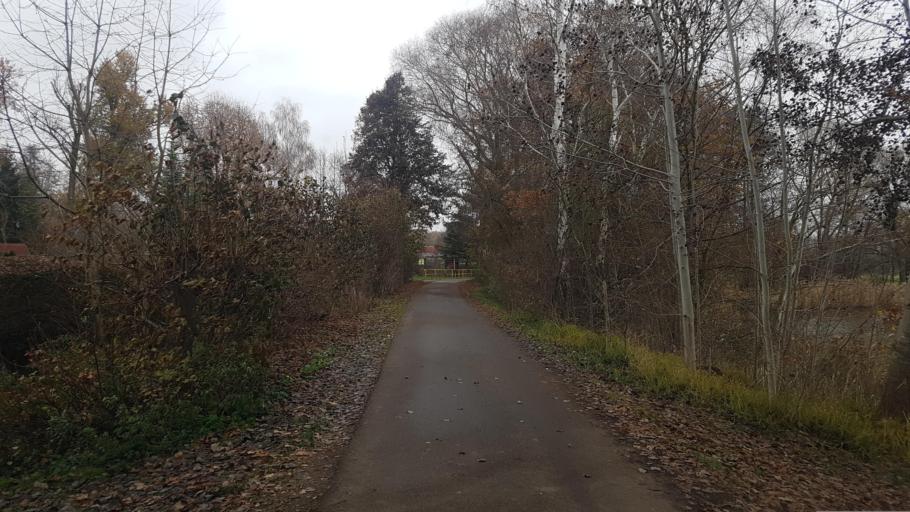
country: DE
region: Brandenburg
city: Lubbenau
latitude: 51.8307
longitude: 13.9319
